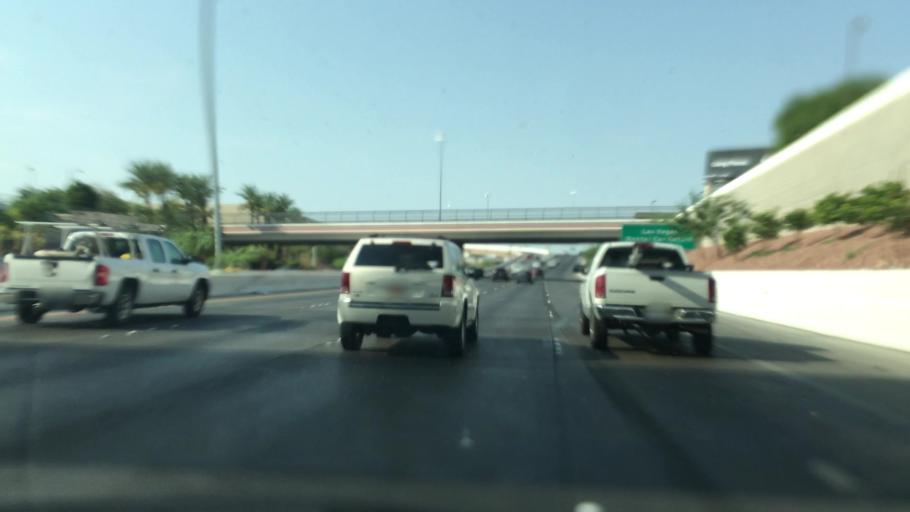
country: US
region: Nevada
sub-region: Clark County
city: Paradise
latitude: 36.0687
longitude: -115.1475
